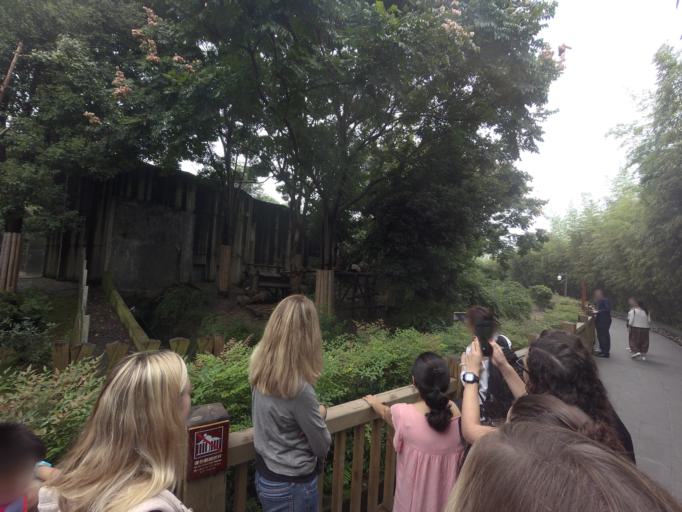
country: CN
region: Sichuan
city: Xindu
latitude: 30.7422
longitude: 104.1375
